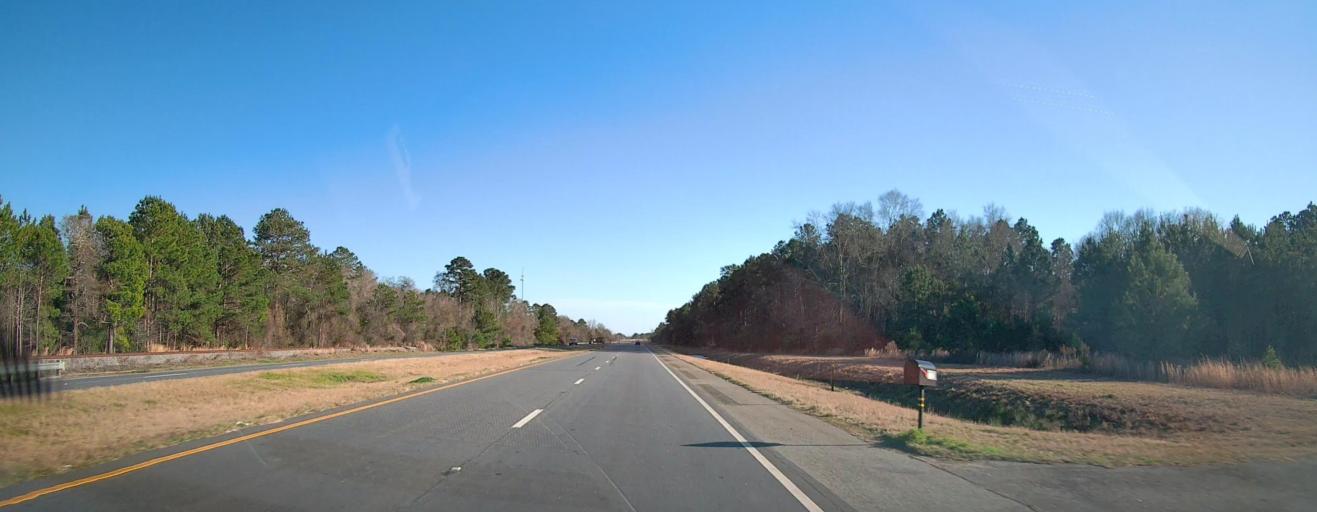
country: US
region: Georgia
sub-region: Lee County
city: Leesburg
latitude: 31.8360
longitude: -84.2215
